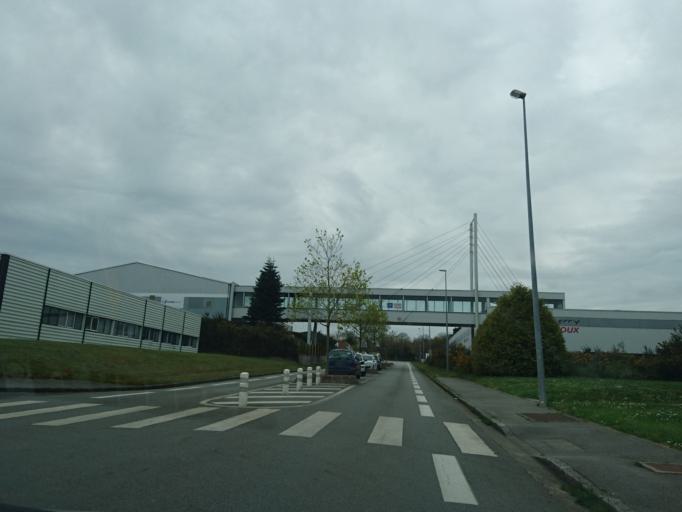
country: FR
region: Brittany
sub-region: Departement du Finistere
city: Roscanvel
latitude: 48.3625
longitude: -4.5667
